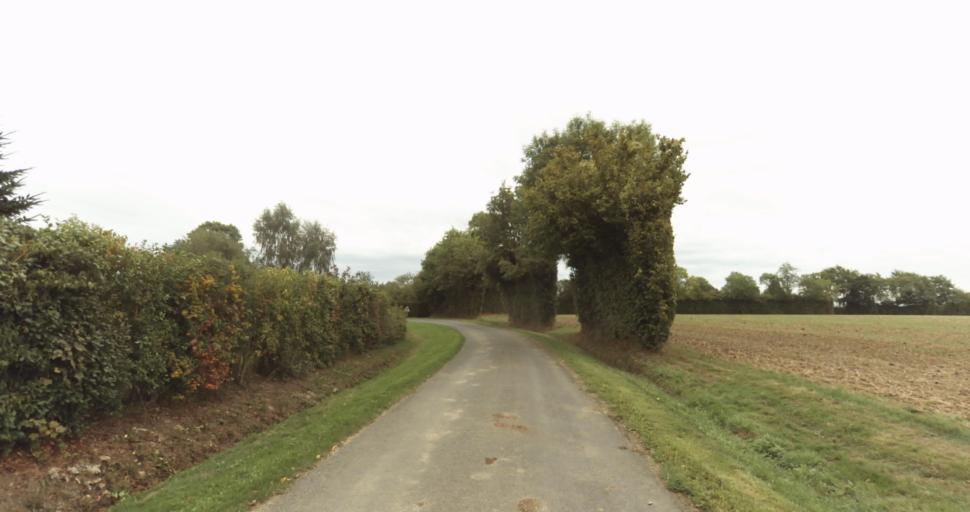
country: FR
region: Lower Normandy
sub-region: Departement de l'Orne
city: Sees
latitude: 48.6760
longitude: 0.2595
